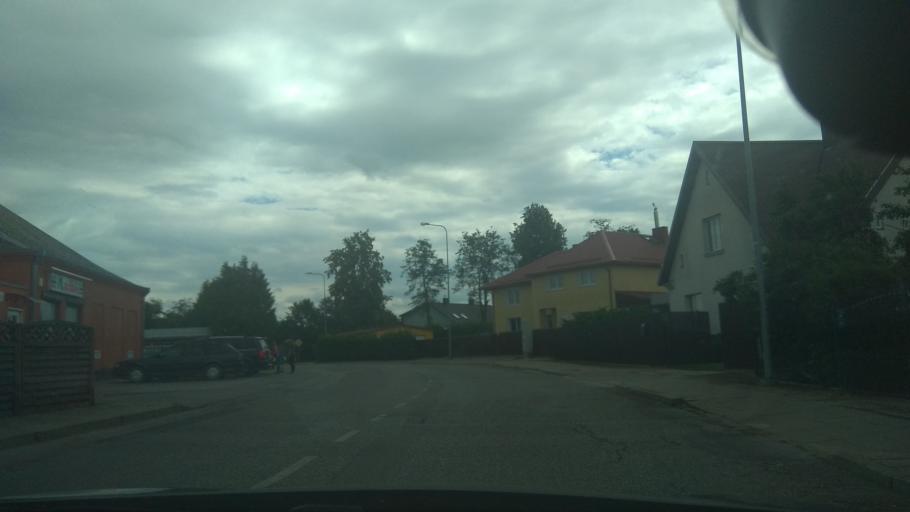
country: LT
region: Marijampoles apskritis
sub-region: Marijampole Municipality
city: Marijampole
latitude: 54.5500
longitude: 23.3535
